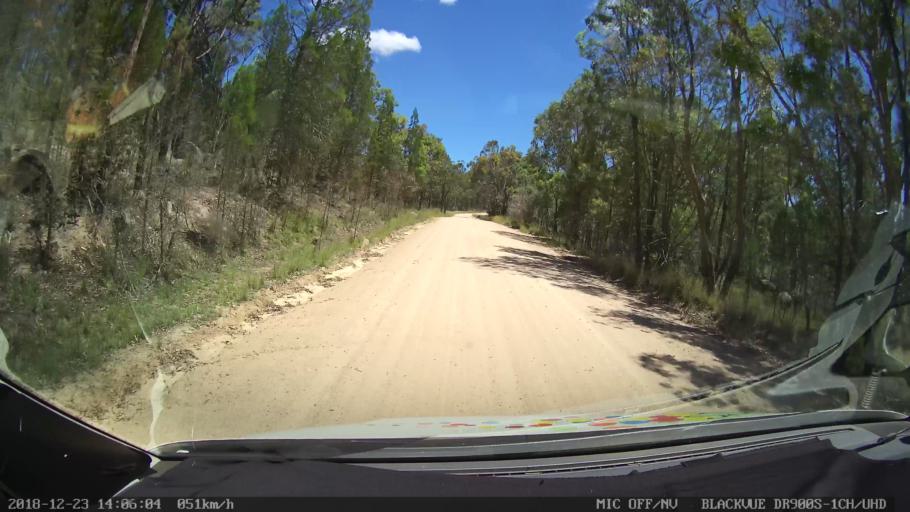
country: AU
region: New South Wales
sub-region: Tamworth Municipality
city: Manilla
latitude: -30.6281
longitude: 151.0770
